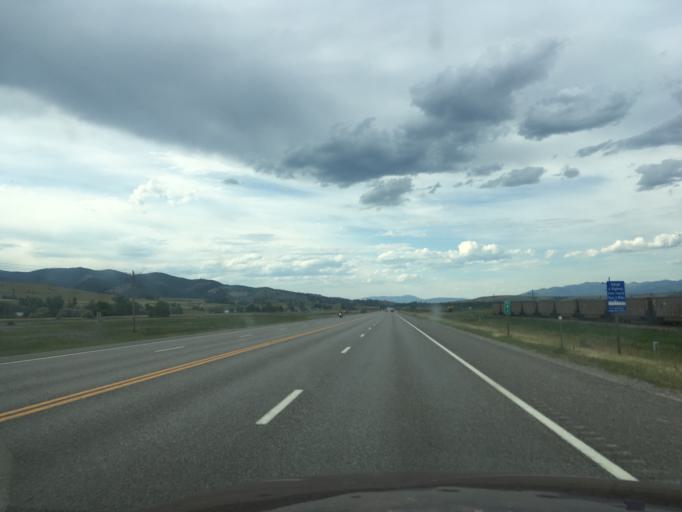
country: US
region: Montana
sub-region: Missoula County
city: Lolo
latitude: 46.7196
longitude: -114.0774
